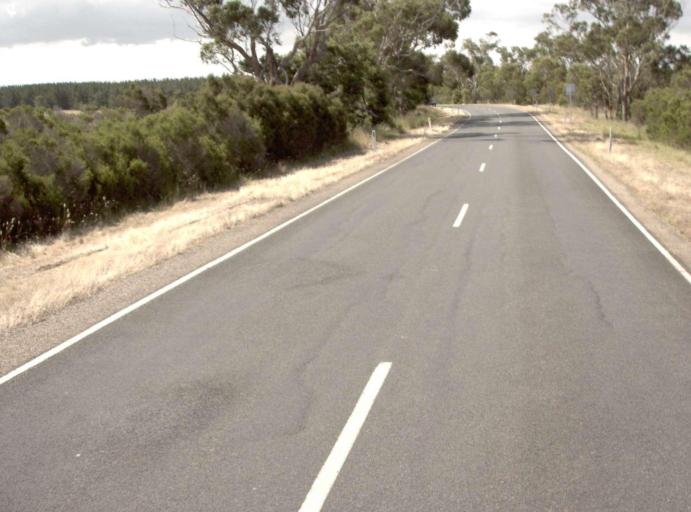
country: AU
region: Victoria
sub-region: Wellington
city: Sale
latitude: -38.2751
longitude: 147.1501
